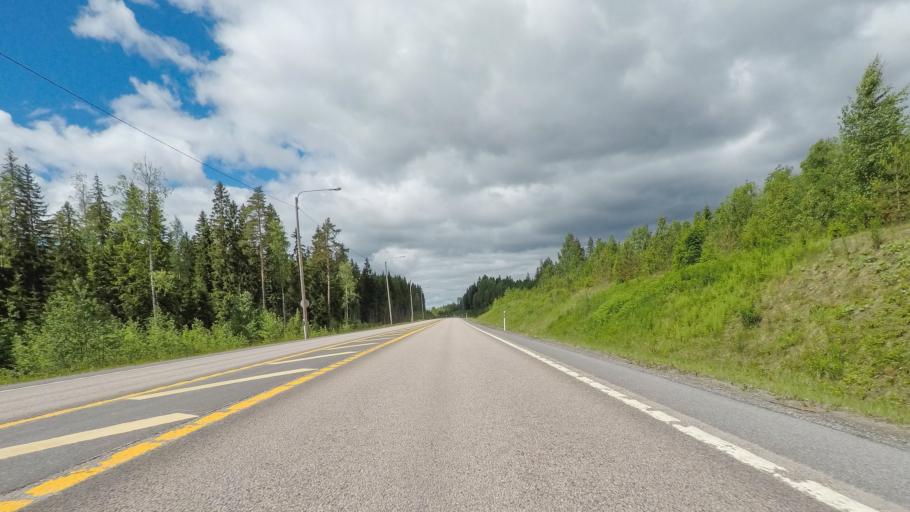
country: FI
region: Paijanne Tavastia
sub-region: Lahti
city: Hartola
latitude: 61.4297
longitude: 26.0100
